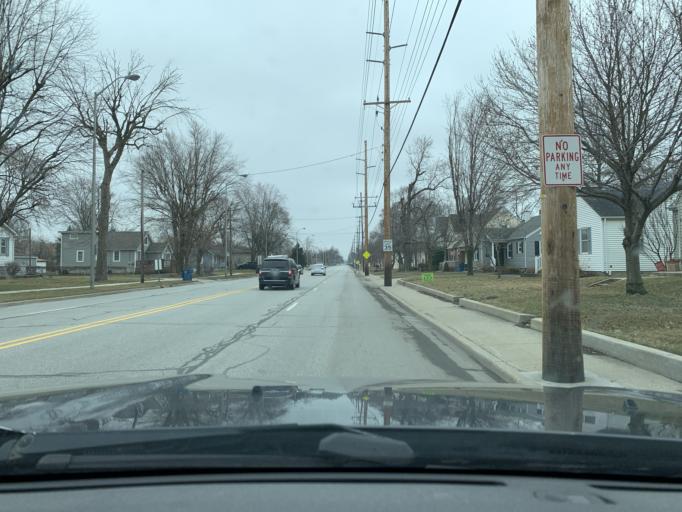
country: US
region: Indiana
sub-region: Lake County
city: Highland
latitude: 41.5501
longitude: -87.4617
